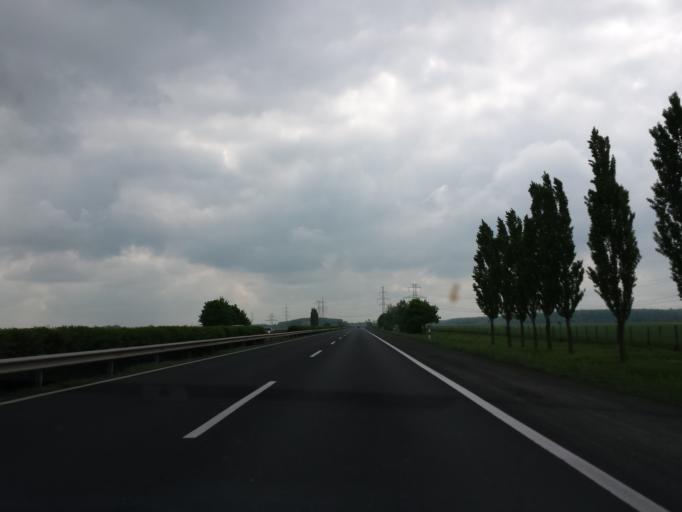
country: HU
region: Gyor-Moson-Sopron
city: Mosonmagyarovar
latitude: 47.8251
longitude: 17.2815
